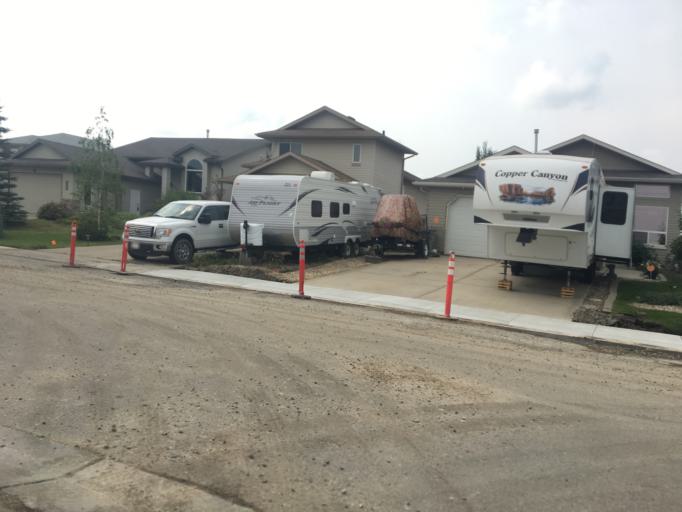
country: CA
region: Alberta
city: Grande Prairie
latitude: 55.1458
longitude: -118.8187
